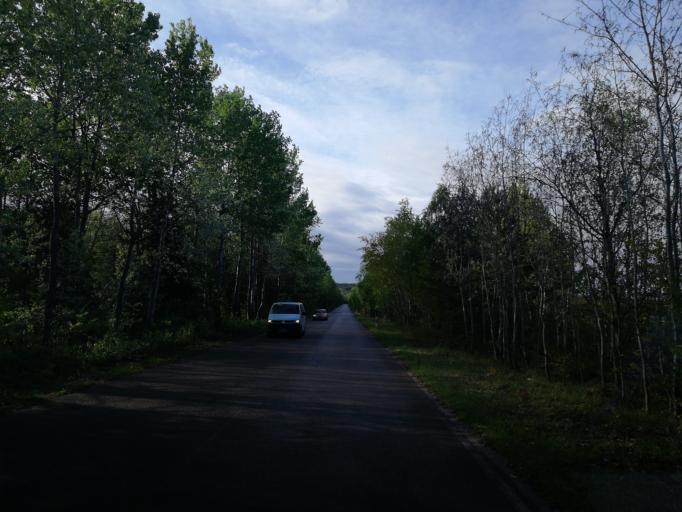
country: DE
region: Brandenburg
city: Lauchhammer
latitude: 51.5320
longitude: 13.7690
